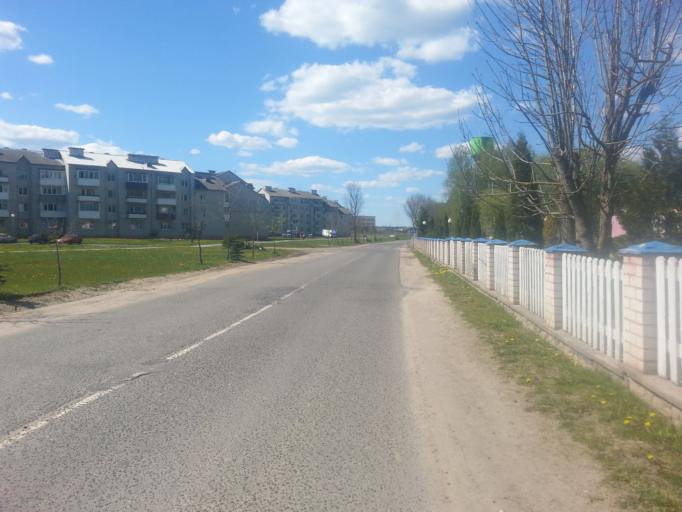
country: BY
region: Minsk
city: Narach
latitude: 54.9164
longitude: 26.7018
